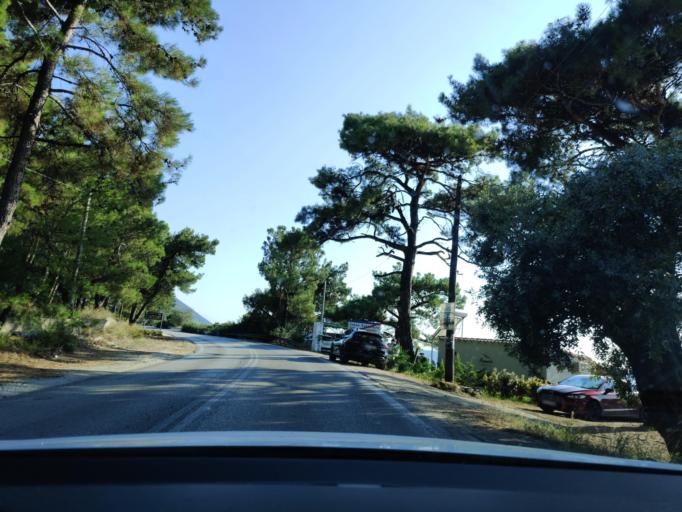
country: GR
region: East Macedonia and Thrace
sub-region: Nomos Kavalas
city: Prinos
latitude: 40.6963
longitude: 24.5254
